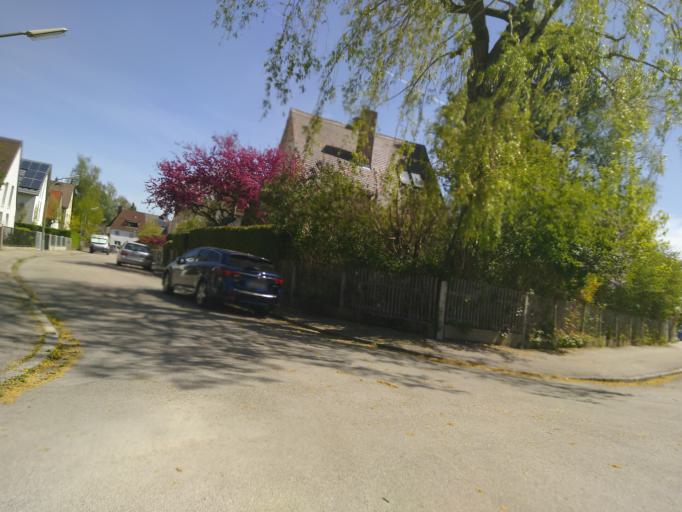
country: DE
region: Bavaria
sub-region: Upper Bavaria
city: Unterhaching
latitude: 48.0960
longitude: 11.6056
